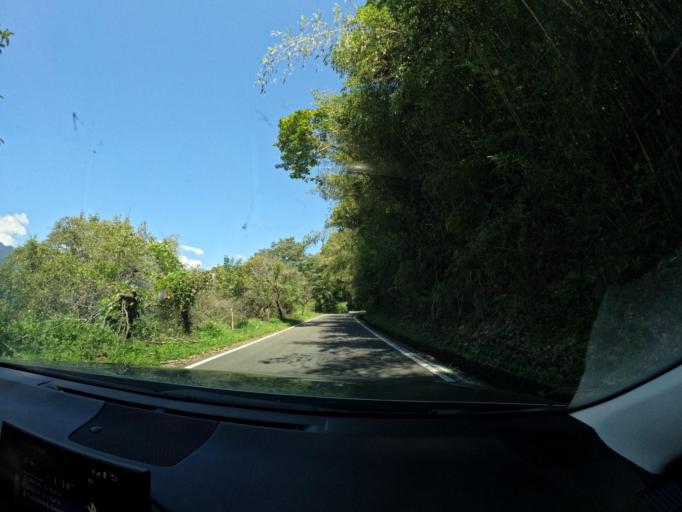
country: TW
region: Taiwan
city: Yujing
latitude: 23.2645
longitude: 120.8506
